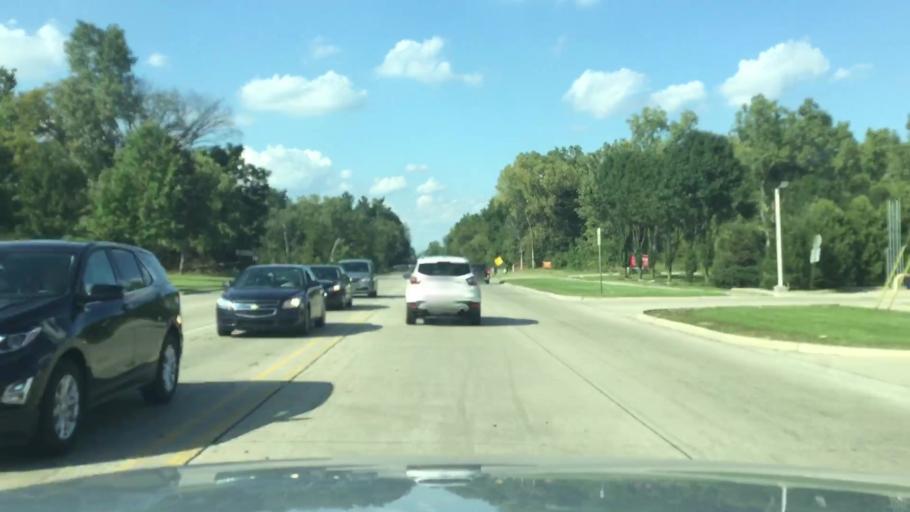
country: US
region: Michigan
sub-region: Wayne County
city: Westland
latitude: 42.3344
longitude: -83.4091
